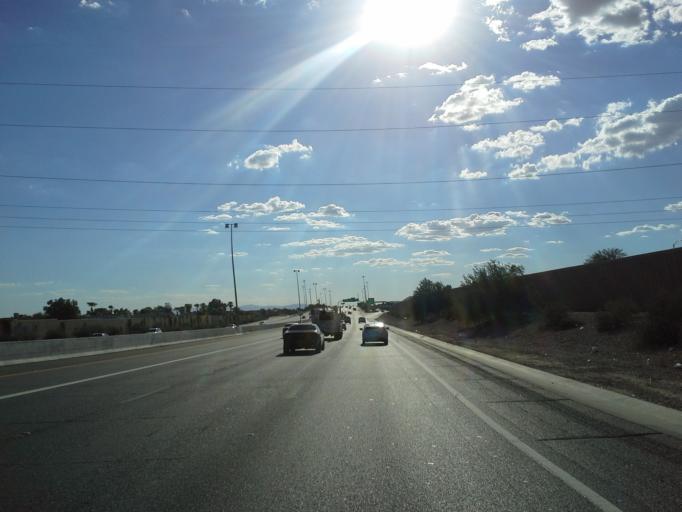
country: US
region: Arizona
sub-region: Maricopa County
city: Paradise Valley
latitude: 33.6693
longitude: -112.0561
